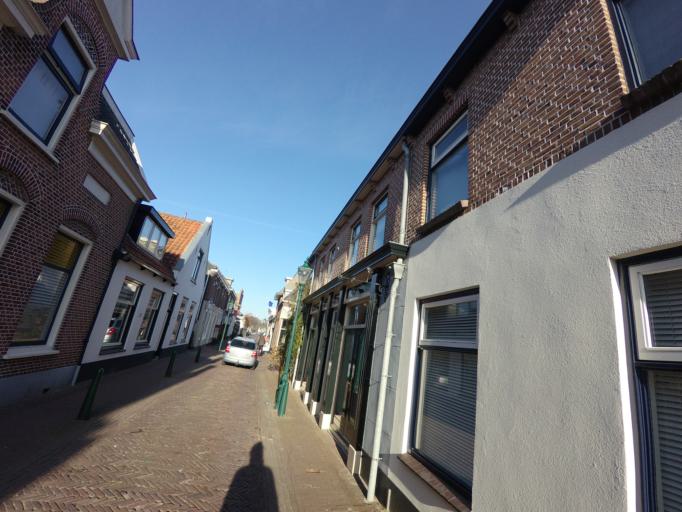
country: NL
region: South Holland
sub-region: Gemeente Teylingen
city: Sassenheim
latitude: 52.1981
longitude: 4.5061
